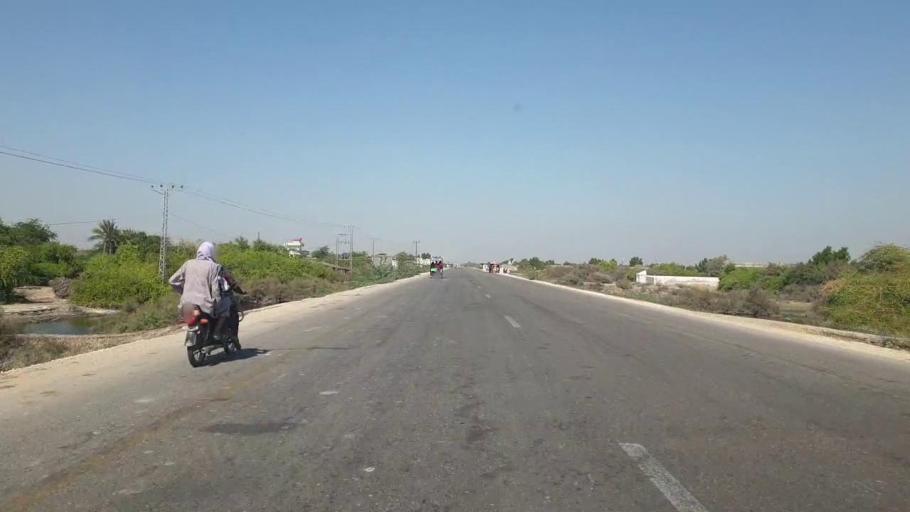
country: PK
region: Sindh
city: Talhar
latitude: 24.8512
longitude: 68.8164
